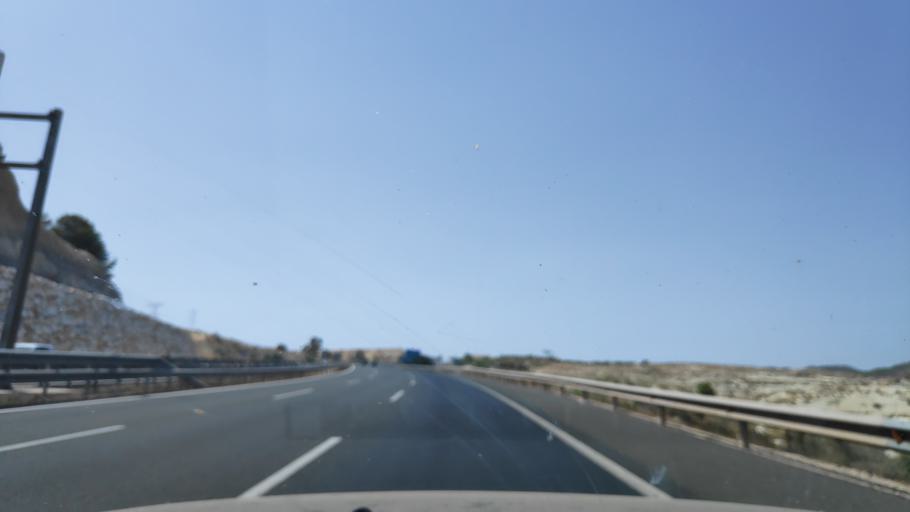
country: ES
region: Murcia
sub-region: Murcia
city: Murcia
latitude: 37.8742
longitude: -1.1272
